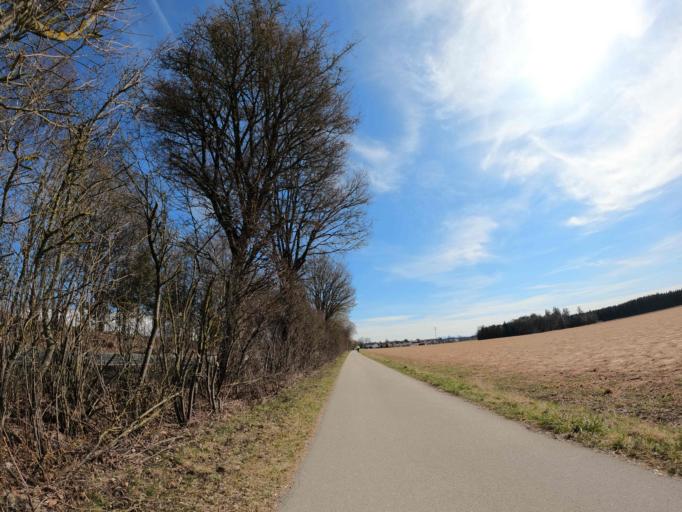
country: DE
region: Bavaria
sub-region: Upper Bavaria
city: Hohenkirchen-Siegertsbrunn
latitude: 48.0254
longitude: 11.6984
